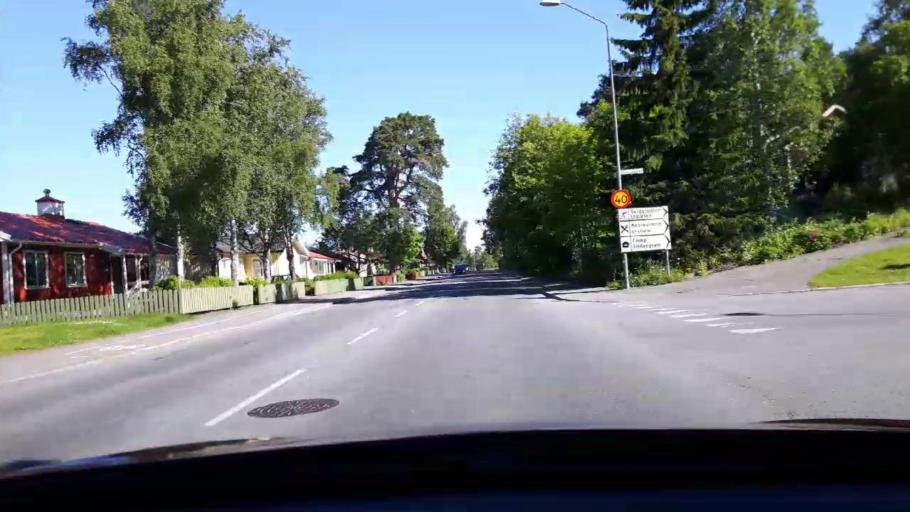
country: SE
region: Jaemtland
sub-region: OEstersunds Kommun
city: Ostersund
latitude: 63.1851
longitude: 14.6538
